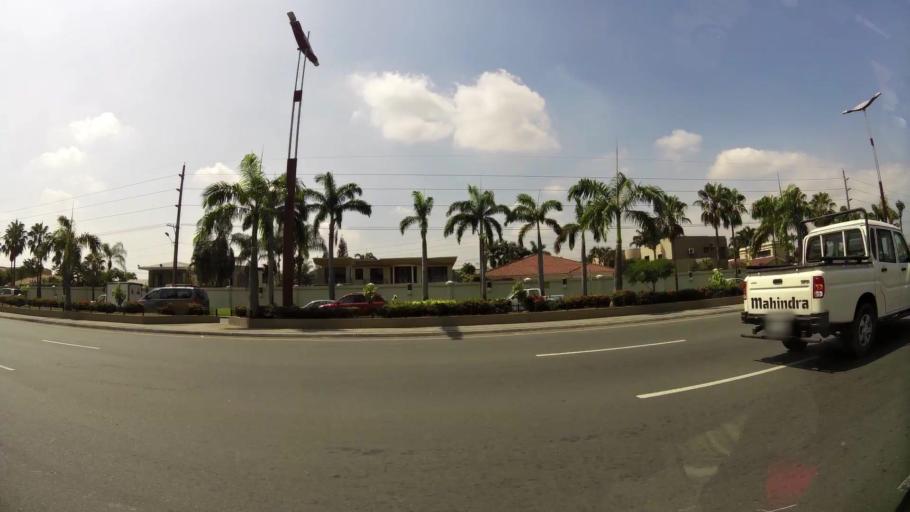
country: EC
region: Guayas
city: Eloy Alfaro
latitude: -2.1294
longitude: -79.8631
